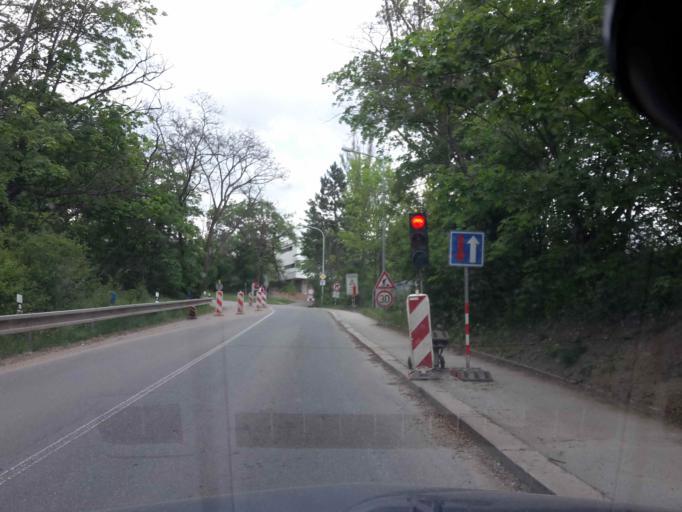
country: CZ
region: South Moravian
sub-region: Mesto Brno
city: Brno
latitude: 49.2267
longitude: 16.6049
